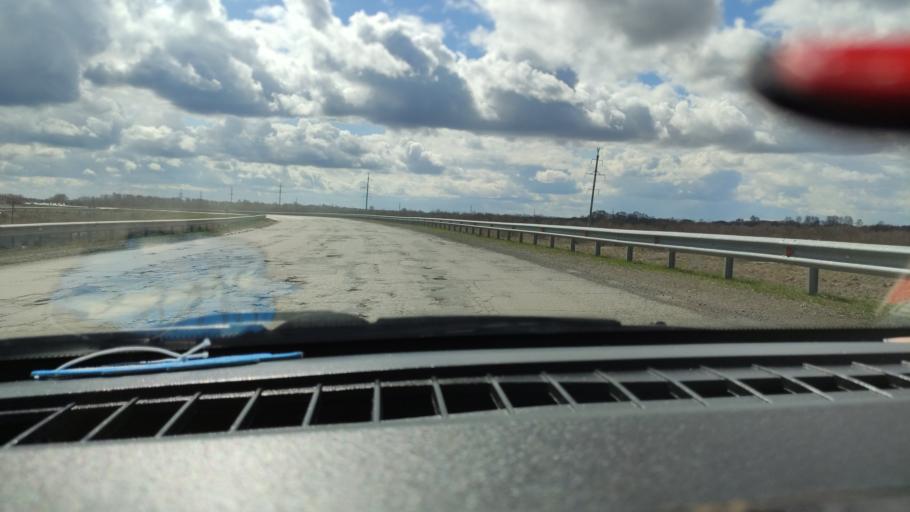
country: RU
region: Samara
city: Tol'yatti
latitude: 53.6679
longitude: 49.4172
